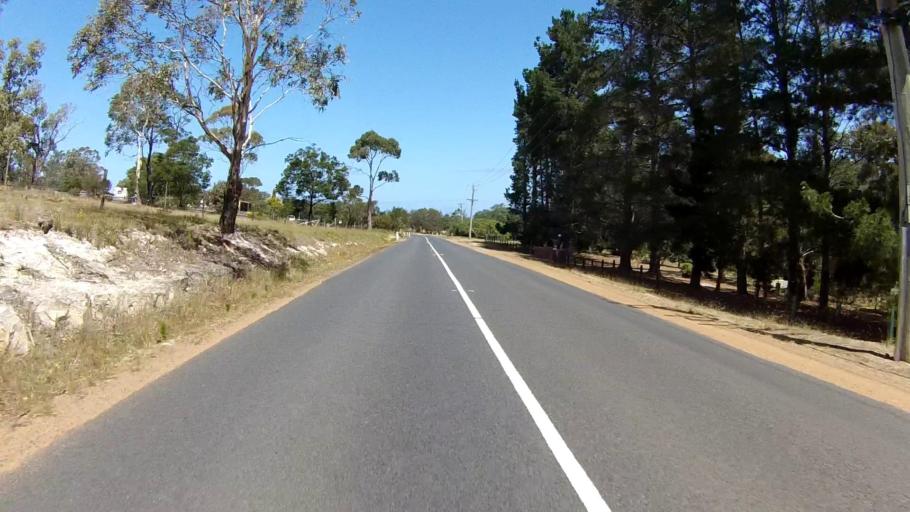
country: AU
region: Tasmania
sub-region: Clarence
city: Sandford
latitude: -42.9615
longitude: 147.4742
